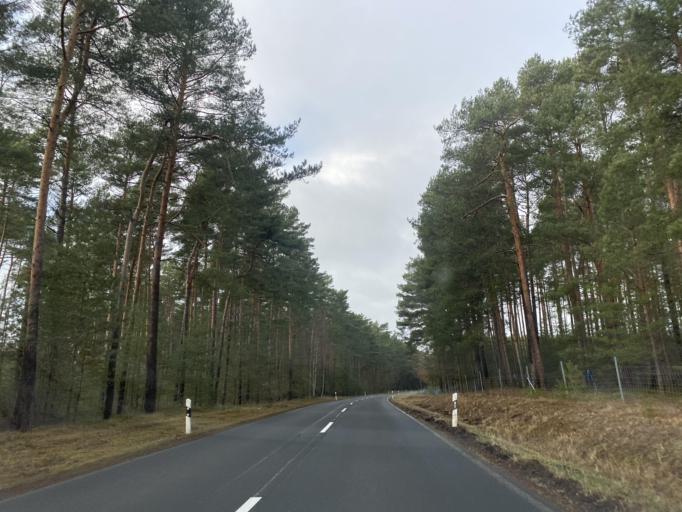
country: PL
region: Lubusz
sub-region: Powiat zarski
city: Leknica
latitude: 51.5070
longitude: 14.7917
